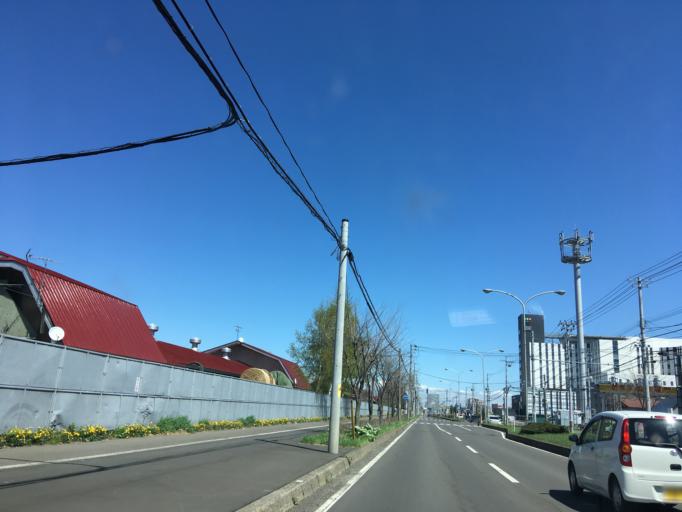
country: JP
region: Hokkaido
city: Obihiro
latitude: 42.9202
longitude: 143.1771
